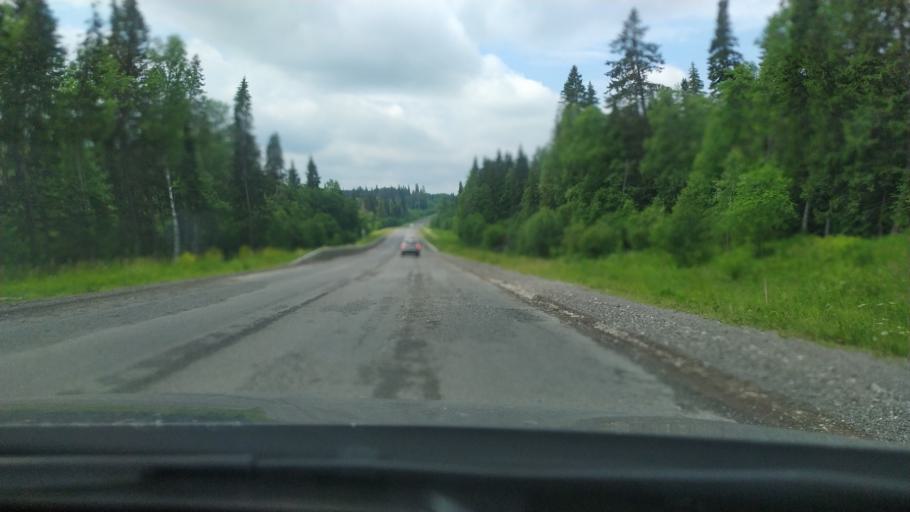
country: RU
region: Perm
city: Kalino
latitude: 58.2783
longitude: 57.3986
